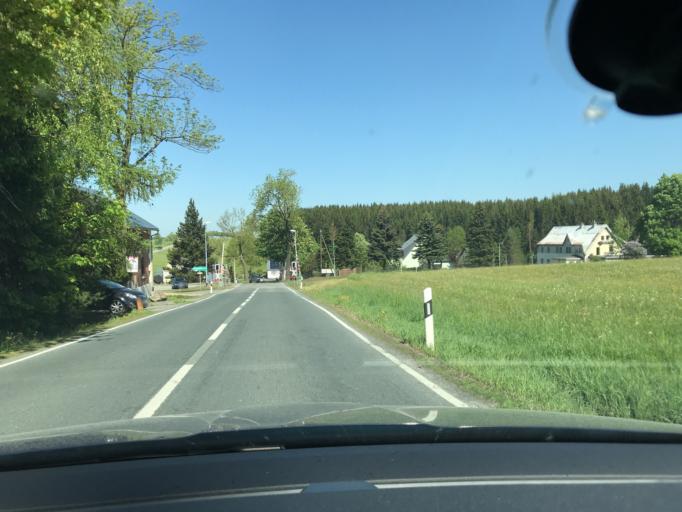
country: CZ
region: Ustecky
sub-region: Okres Chomutov
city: Vejprty
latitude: 50.4669
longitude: 12.9895
